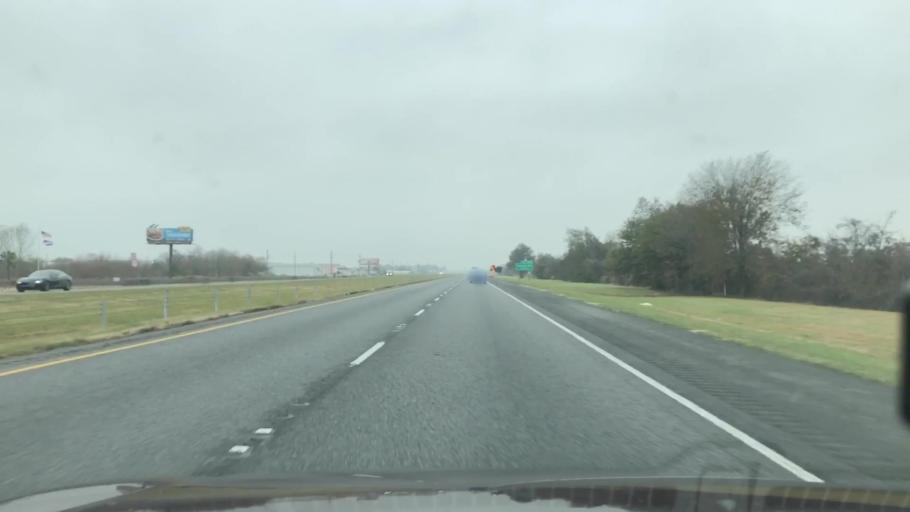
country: US
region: Louisiana
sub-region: Ouachita Parish
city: Lakeshore
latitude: 32.4911
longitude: -92.0136
